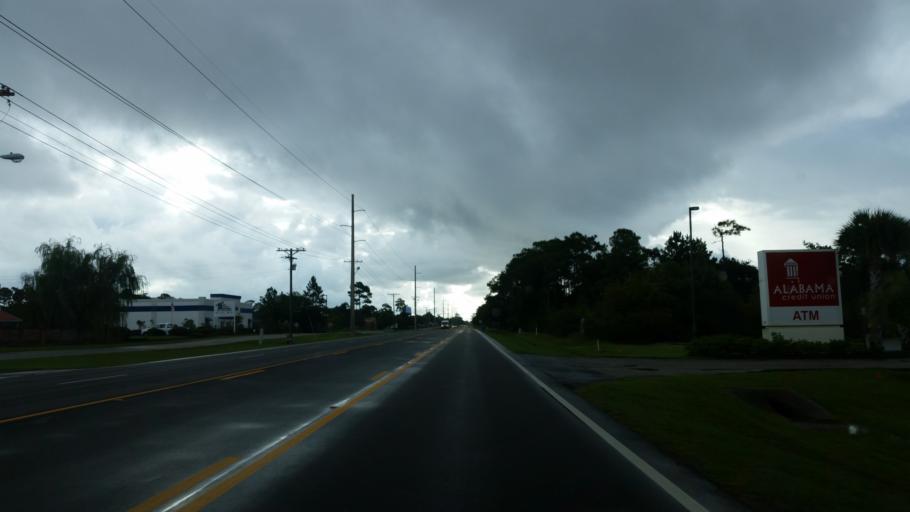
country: US
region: Alabama
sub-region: Baldwin County
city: Orange Beach
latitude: 30.2902
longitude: -87.6106
